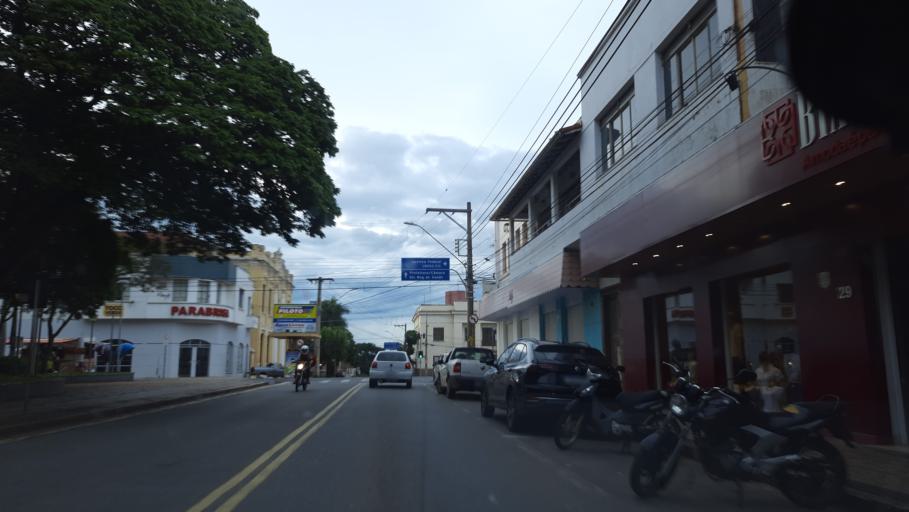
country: BR
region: Sao Paulo
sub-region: Sao Joao Da Boa Vista
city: Sao Joao da Boa Vista
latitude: -21.9702
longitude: -46.7983
